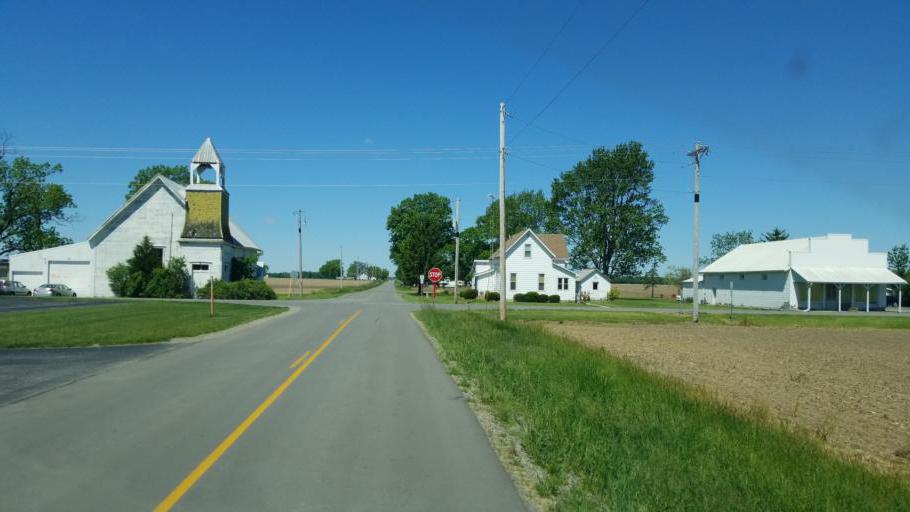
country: US
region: Ohio
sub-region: Logan County
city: Lakeview
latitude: 40.4174
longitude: -83.9454
